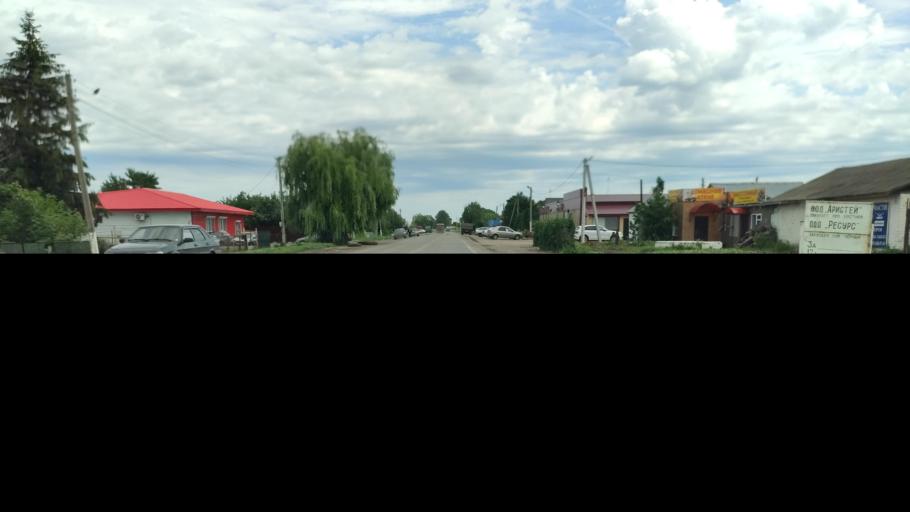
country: RU
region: Voronezj
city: Panino
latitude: 51.6573
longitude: 40.1255
